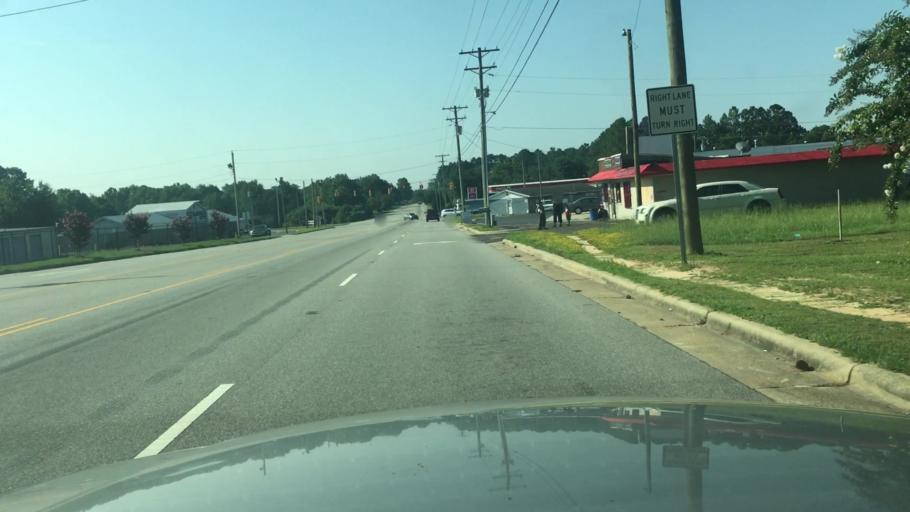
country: US
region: North Carolina
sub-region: Cumberland County
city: Spring Lake
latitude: 35.1524
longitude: -78.9125
